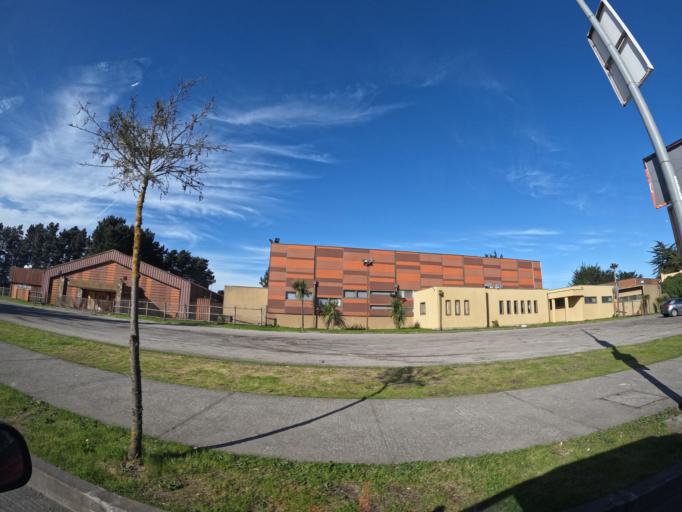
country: CL
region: Biobio
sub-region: Provincia de Concepcion
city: Concepcion
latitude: -36.7753
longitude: -73.0690
